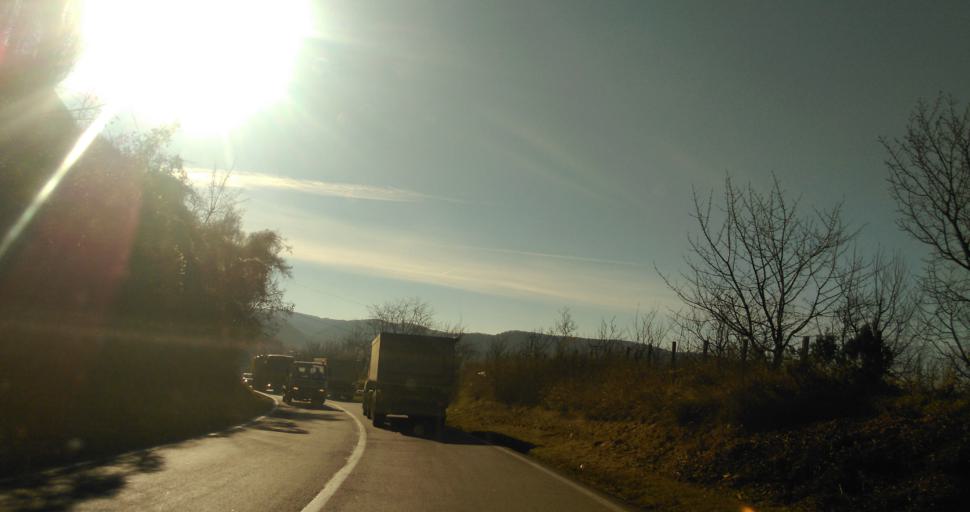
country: RS
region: Autonomna Pokrajina Vojvodina
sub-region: Juznobacki Okrug
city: Novi Sad
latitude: 45.2096
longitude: 19.8443
